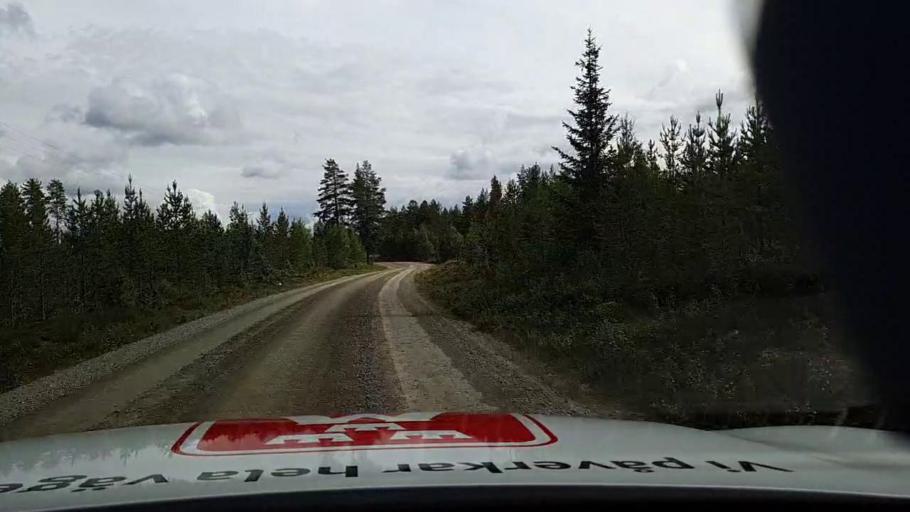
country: SE
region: Jaemtland
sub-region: Are Kommun
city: Jarpen
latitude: 62.5060
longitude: 13.4981
